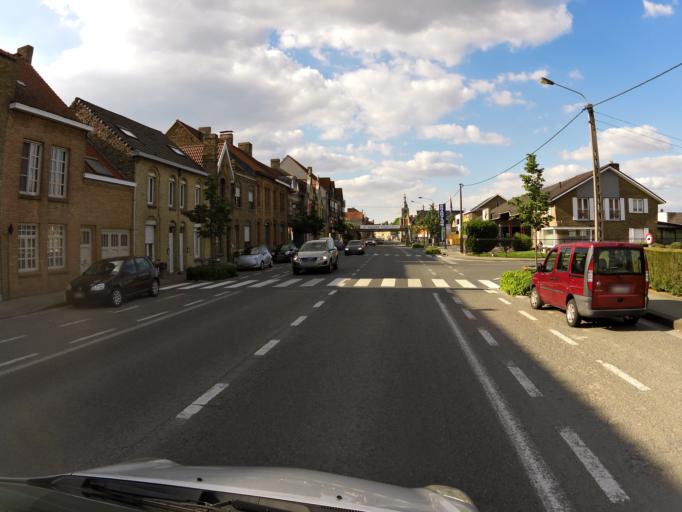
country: BE
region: Flanders
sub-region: Provincie West-Vlaanderen
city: Diksmuide
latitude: 51.0285
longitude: 2.8640
